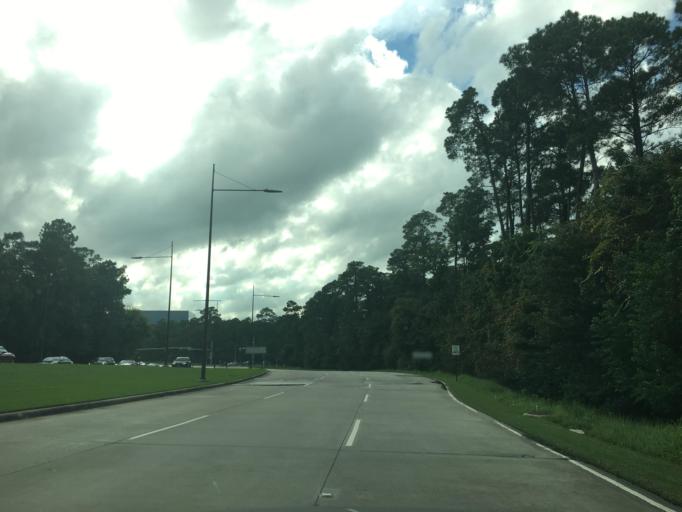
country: US
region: Texas
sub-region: Harris County
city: Spring
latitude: 30.1056
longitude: -95.4373
